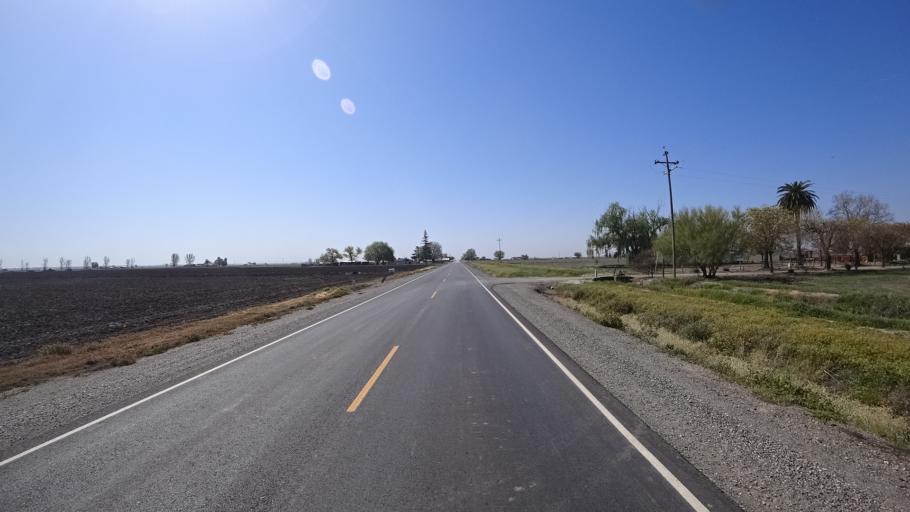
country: US
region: California
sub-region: Glenn County
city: Willows
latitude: 39.5708
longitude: -122.0652
